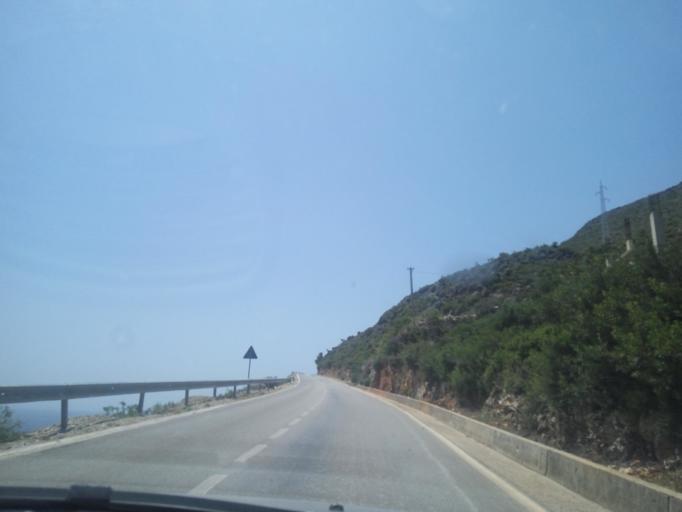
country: AL
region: Vlore
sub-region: Rrethi i Sarandes
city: Lukove
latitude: 40.0579
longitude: 19.8465
